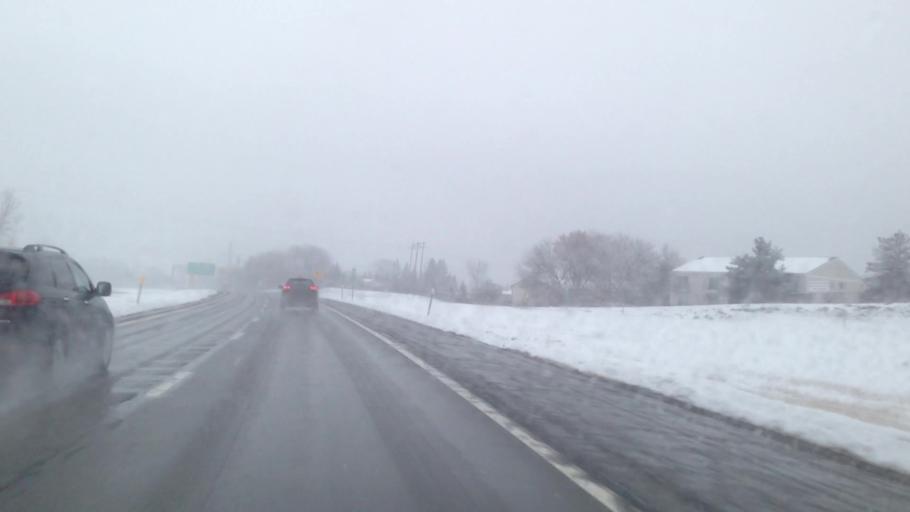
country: US
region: New York
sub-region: Onondaga County
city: Fairmount
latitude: 43.0578
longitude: -76.2367
